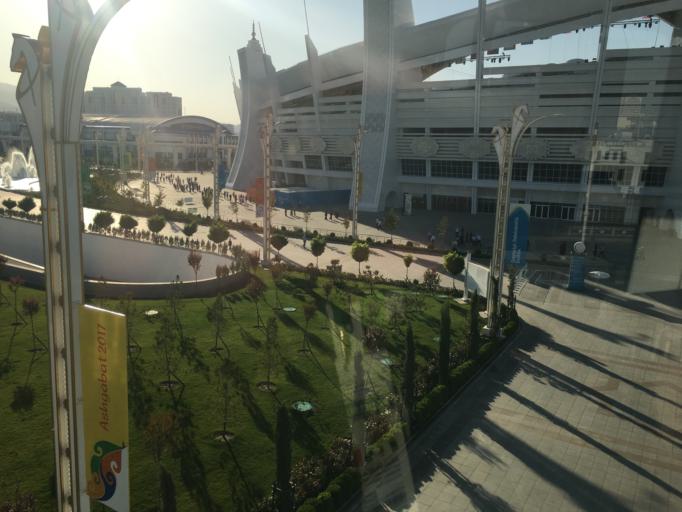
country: TM
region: Ahal
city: Ashgabat
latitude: 37.9030
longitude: 58.3792
